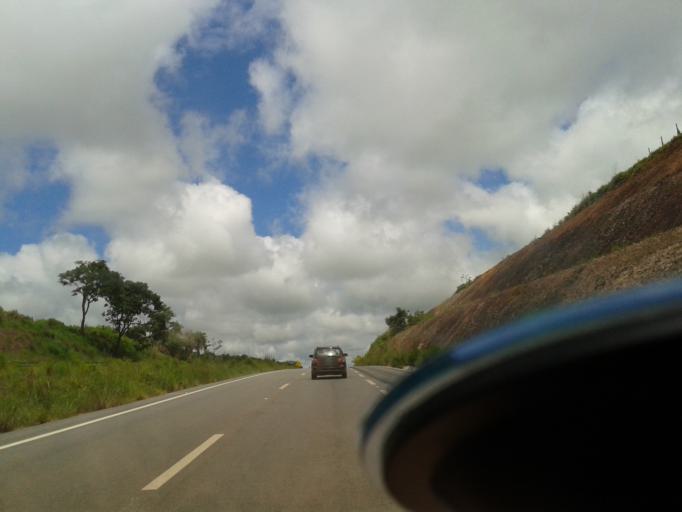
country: BR
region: Goias
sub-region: Itaberai
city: Itaberai
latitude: -16.1571
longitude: -49.6263
